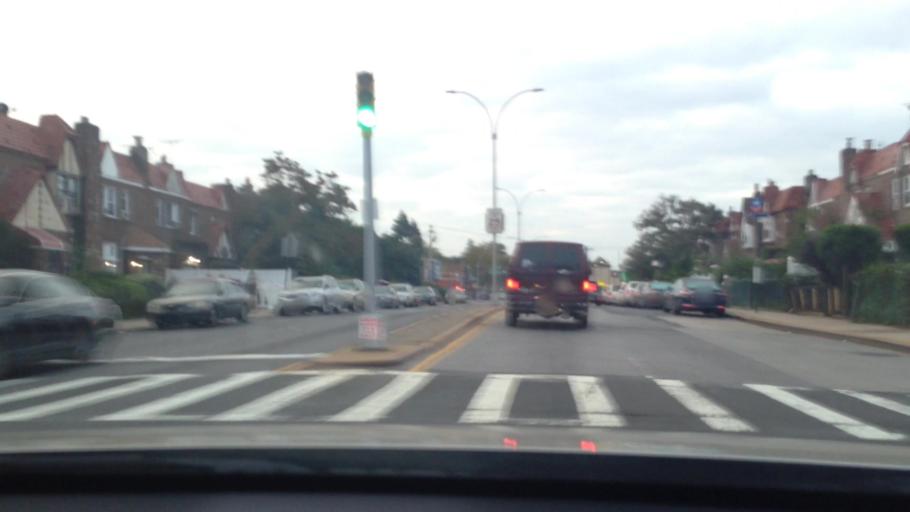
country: US
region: New York
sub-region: Nassau County
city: Bellerose Terrace
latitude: 40.7088
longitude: -73.7519
